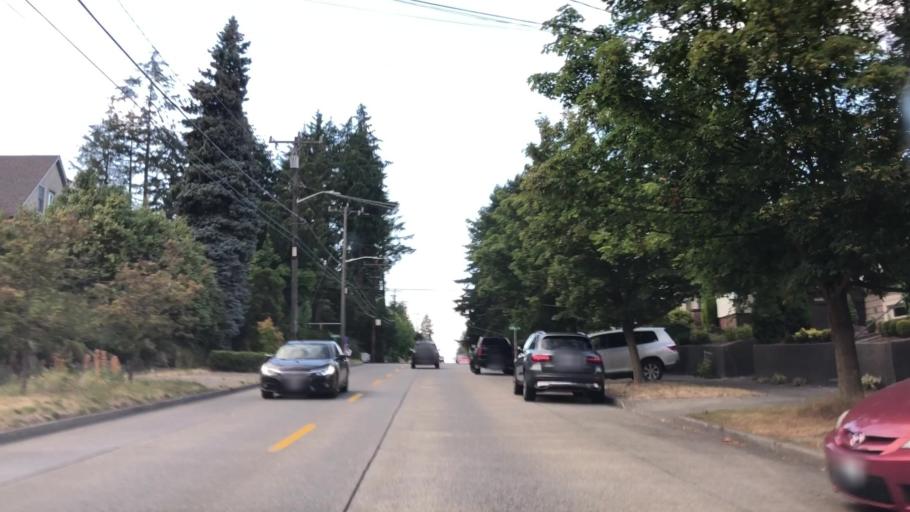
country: US
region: Washington
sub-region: King County
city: Shoreline
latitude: 47.6895
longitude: -122.3122
